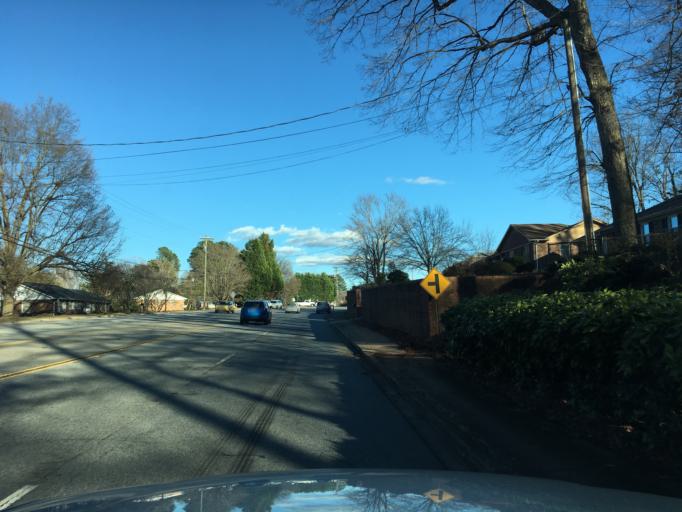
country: US
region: South Carolina
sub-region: Greenville County
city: Wade Hampton
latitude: 34.8723
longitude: -82.3360
